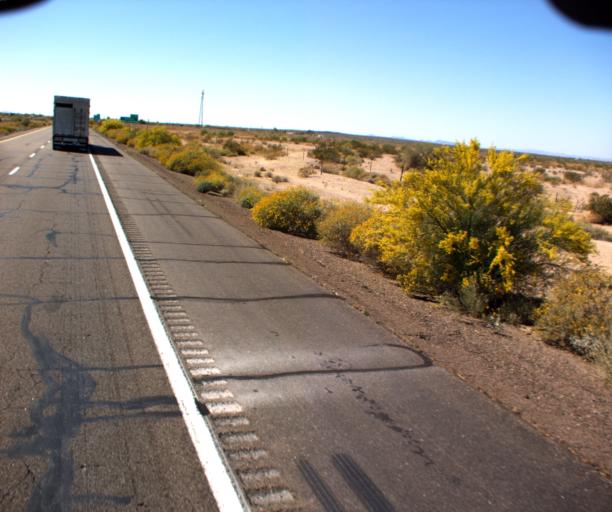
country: US
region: Arizona
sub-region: Maricopa County
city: Gila Bend
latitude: 32.8603
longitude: -113.1954
